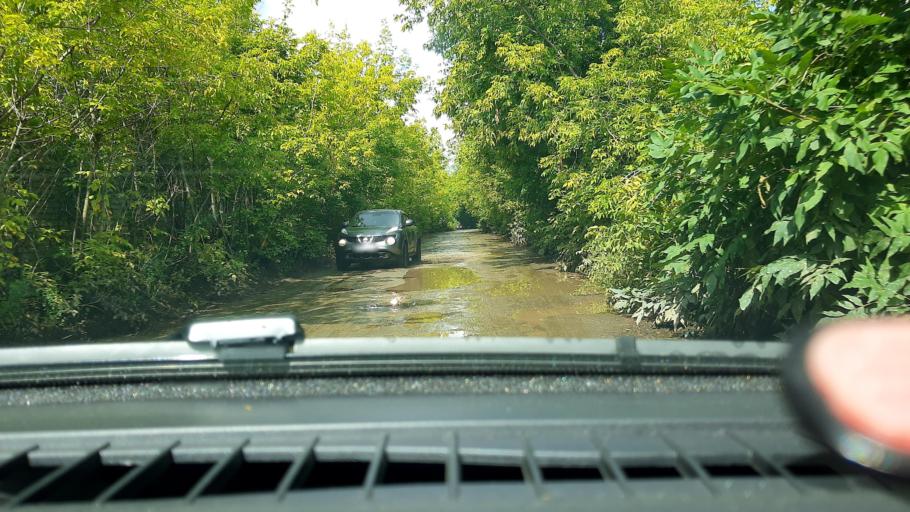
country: RU
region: Nizjnij Novgorod
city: Gorbatovka
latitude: 56.2545
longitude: 43.8327
